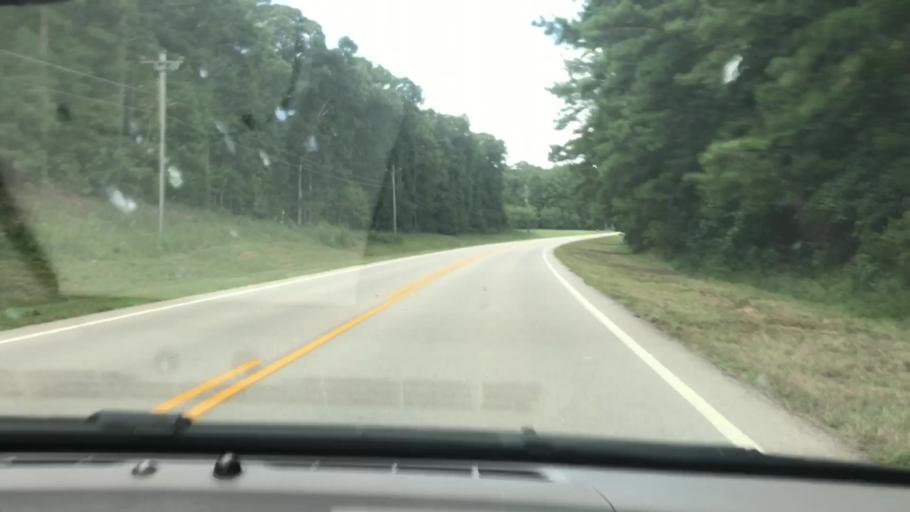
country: US
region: Georgia
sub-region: Troup County
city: La Grange
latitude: 33.1021
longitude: -85.0706
